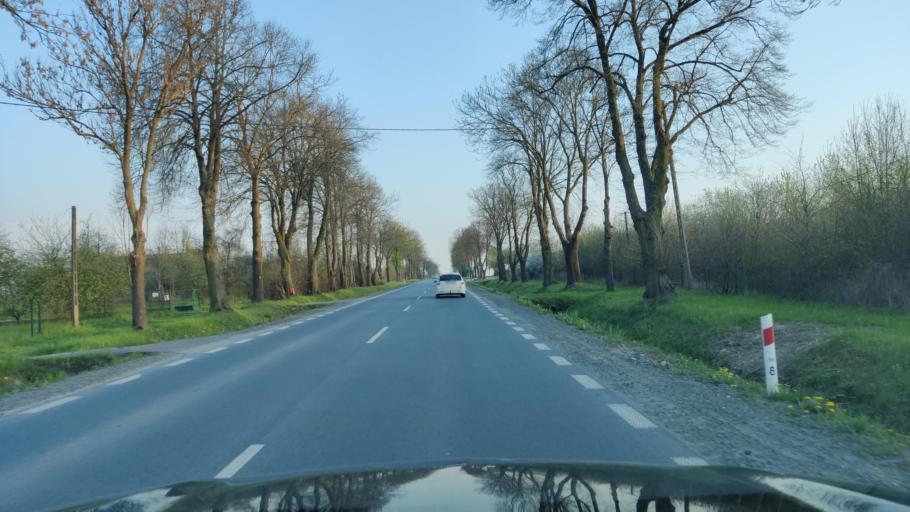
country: PL
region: Masovian Voivodeship
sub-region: Powiat pultuski
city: Pultusk
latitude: 52.6844
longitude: 21.0807
